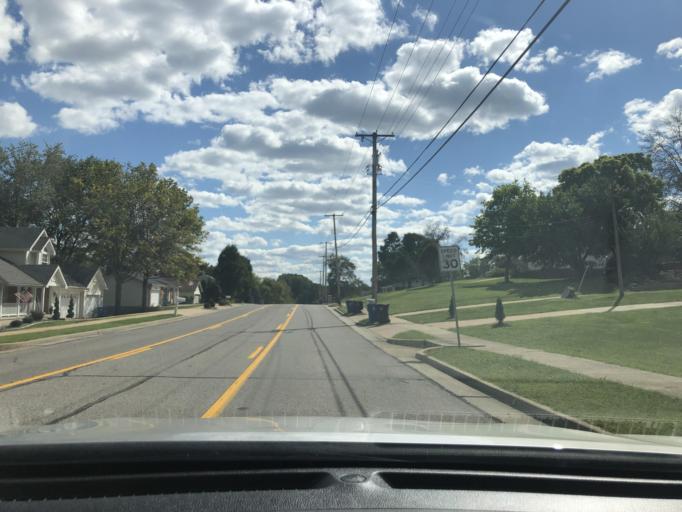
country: US
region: Missouri
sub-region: Saint Louis County
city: Green Park
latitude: 38.5098
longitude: -90.3429
